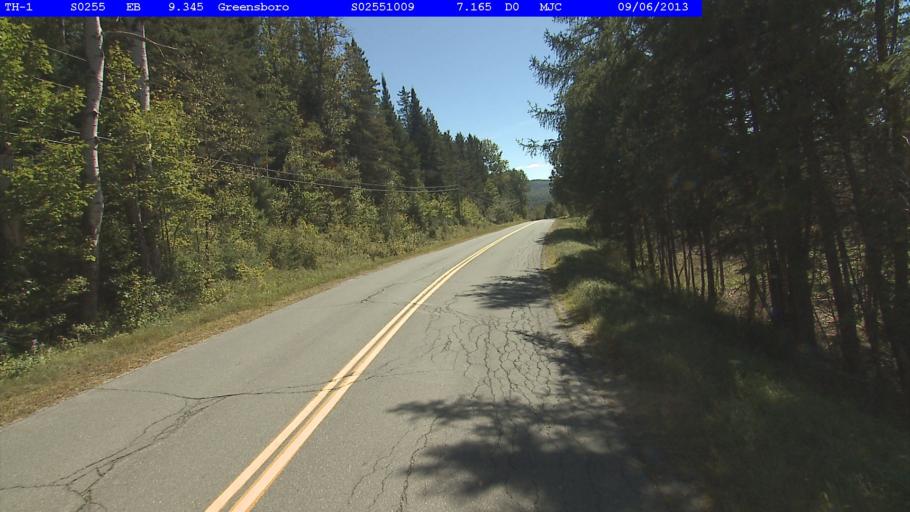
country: US
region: Vermont
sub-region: Caledonia County
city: Hardwick
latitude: 44.5524
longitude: -72.2719
